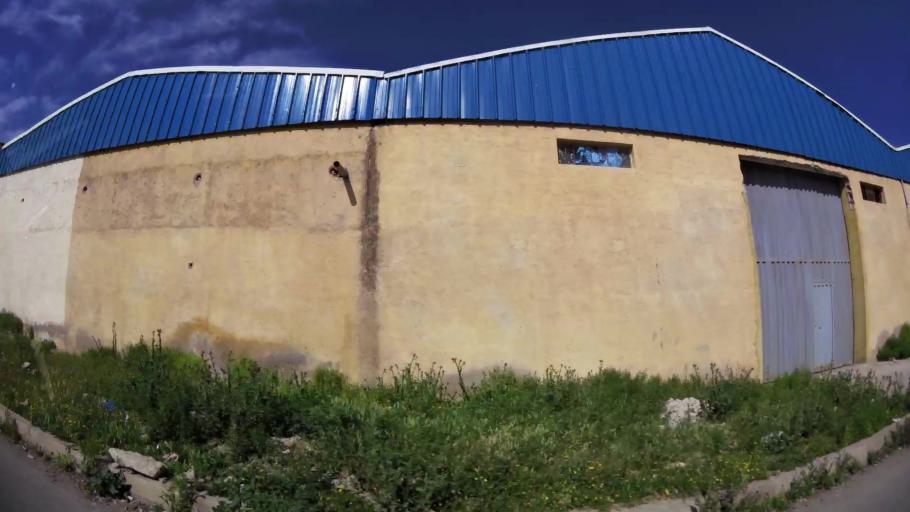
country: MA
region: Oriental
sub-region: Oujda-Angad
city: Oujda
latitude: 34.7050
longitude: -1.8870
